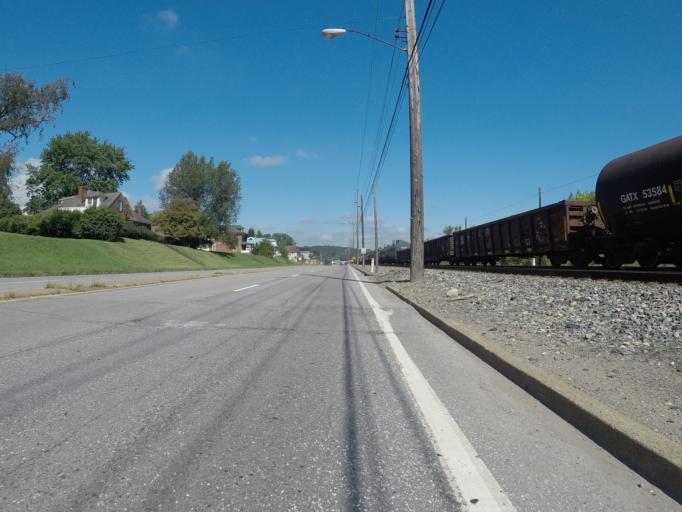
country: US
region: Ohio
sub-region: Lawrence County
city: South Point
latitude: 38.4399
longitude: -82.6090
